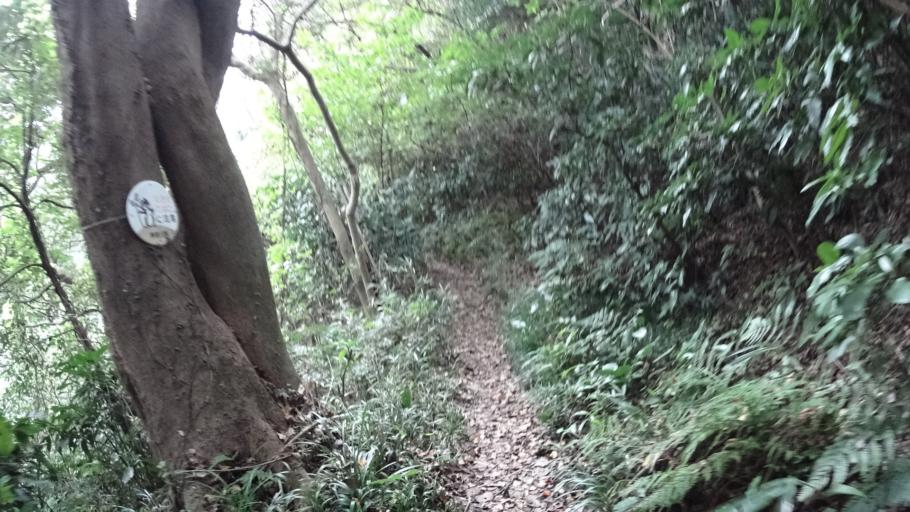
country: JP
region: Kanagawa
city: Zushi
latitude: 35.2870
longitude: 139.6149
